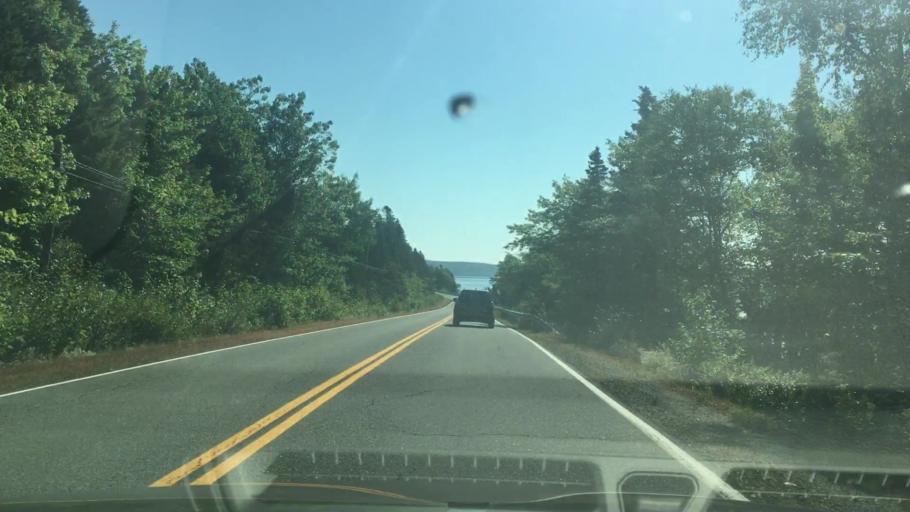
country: CA
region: Nova Scotia
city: Cole Harbour
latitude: 44.8153
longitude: -62.8772
